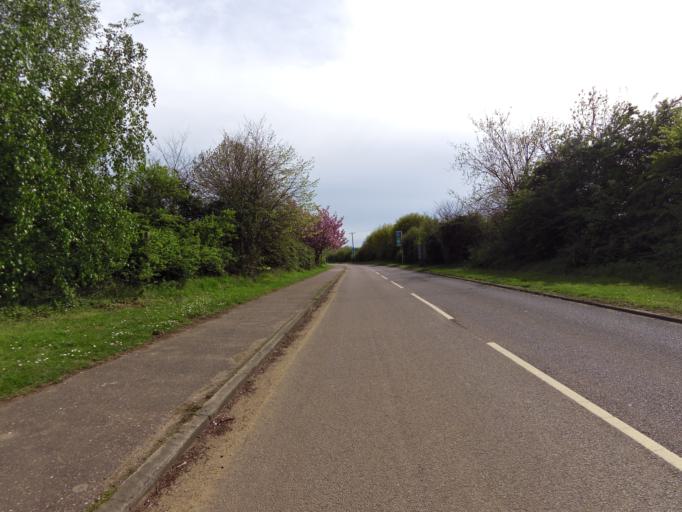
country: GB
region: England
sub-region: Essex
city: Mistley
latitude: 51.9735
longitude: 1.1373
